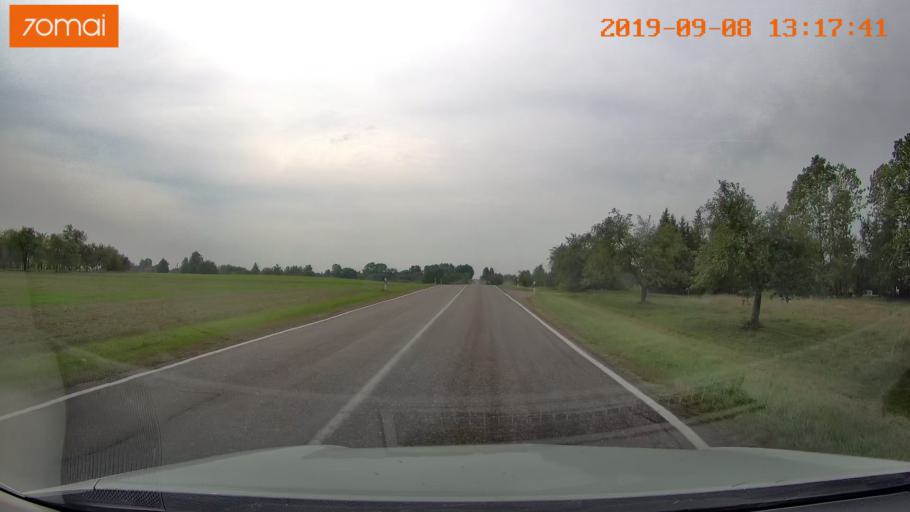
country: LT
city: Jieznas
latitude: 54.7151
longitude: 24.2221
